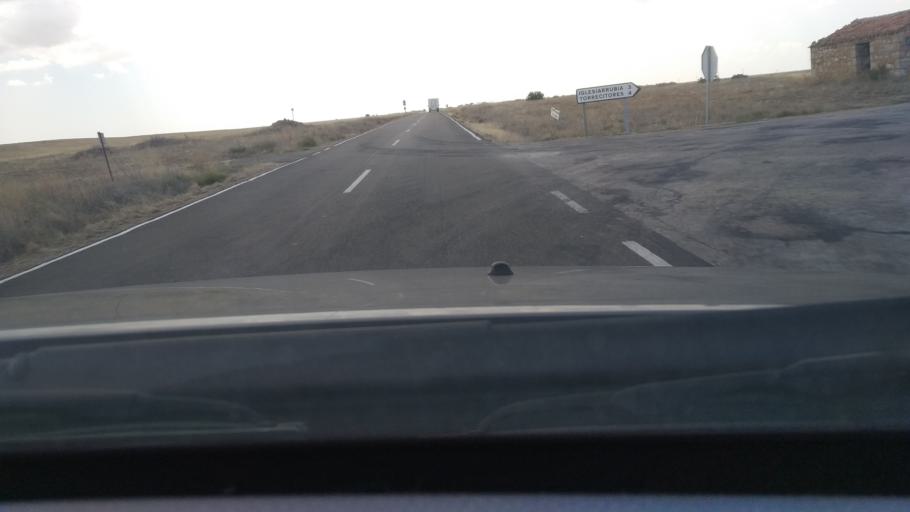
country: ES
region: Castille and Leon
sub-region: Provincia de Burgos
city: Avellanosa de Muno
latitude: 41.9579
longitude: -3.8231
